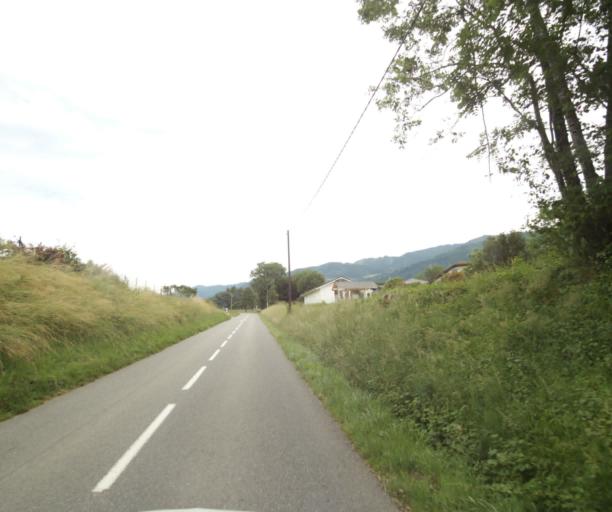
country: FR
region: Rhone-Alpes
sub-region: Departement de la Haute-Savoie
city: Perrignier
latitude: 46.2949
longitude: 6.4262
